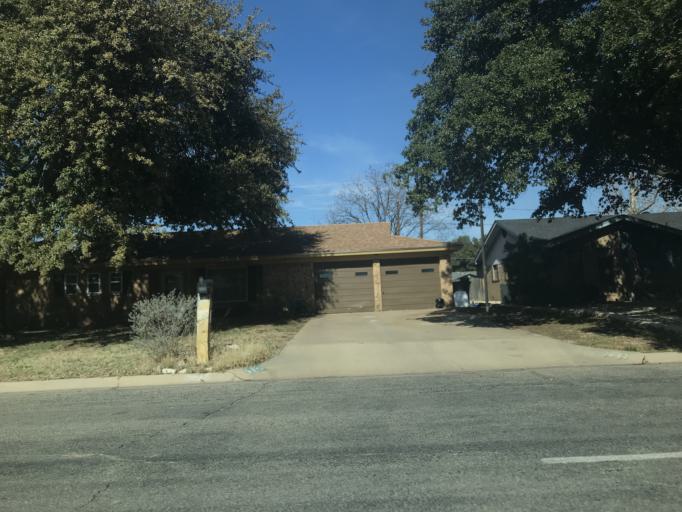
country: US
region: Texas
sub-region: Tom Green County
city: San Angelo
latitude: 31.4313
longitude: -100.4910
